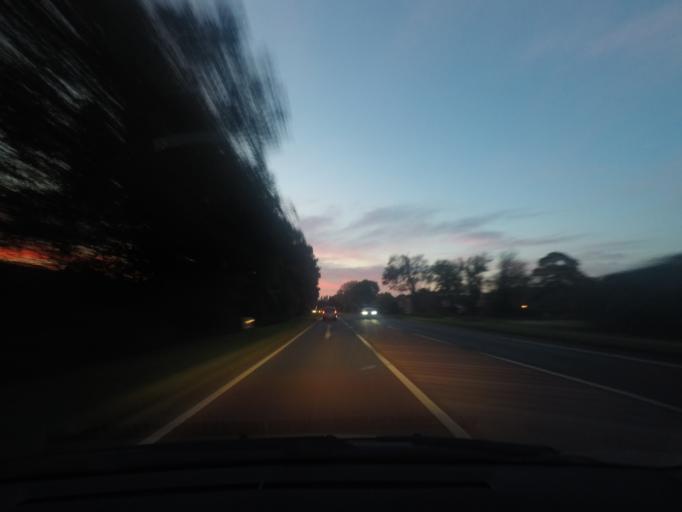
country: GB
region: England
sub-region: East Riding of Yorkshire
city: Pocklington
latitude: 53.9276
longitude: -0.8162
